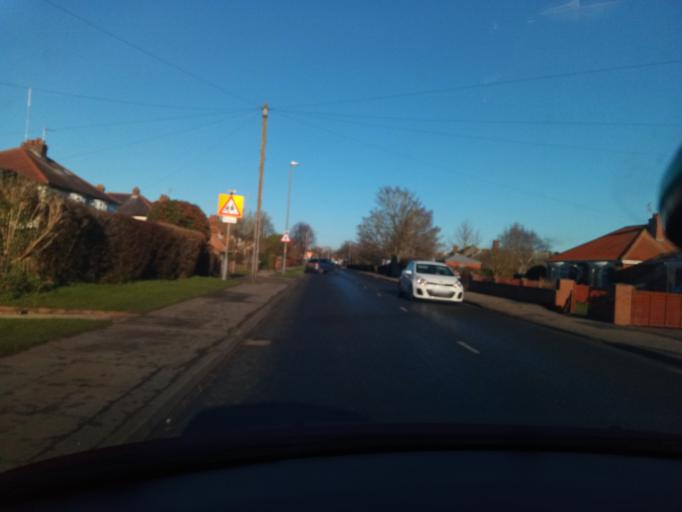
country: GB
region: England
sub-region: North Yorkshire
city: Thirsk
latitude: 54.2255
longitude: -1.3479
